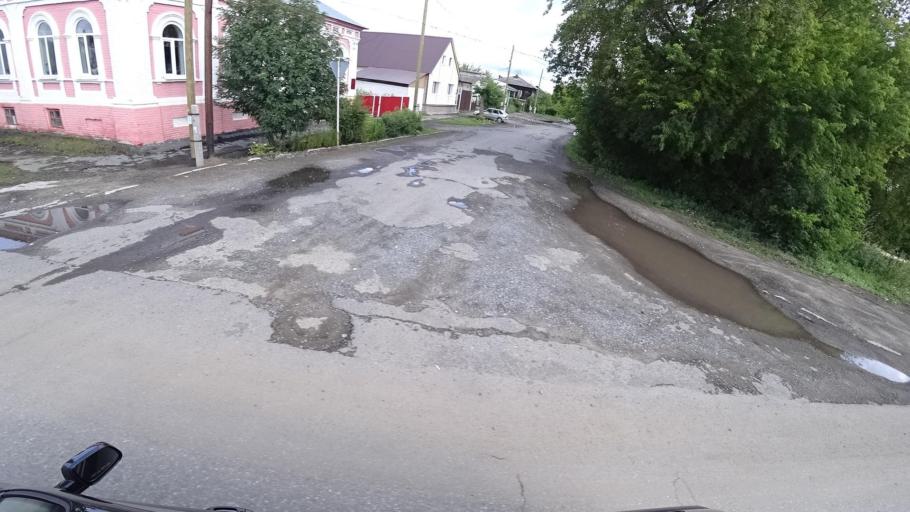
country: RU
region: Sverdlovsk
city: Kamyshlov
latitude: 56.8405
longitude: 62.7038
